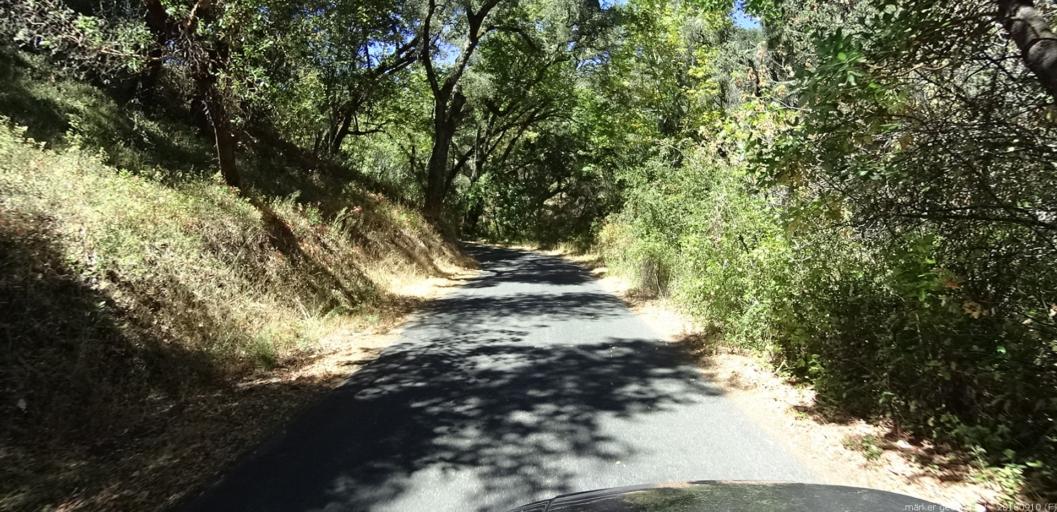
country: US
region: California
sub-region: Monterey County
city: Carmel Valley Village
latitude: 36.4292
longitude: -121.7903
